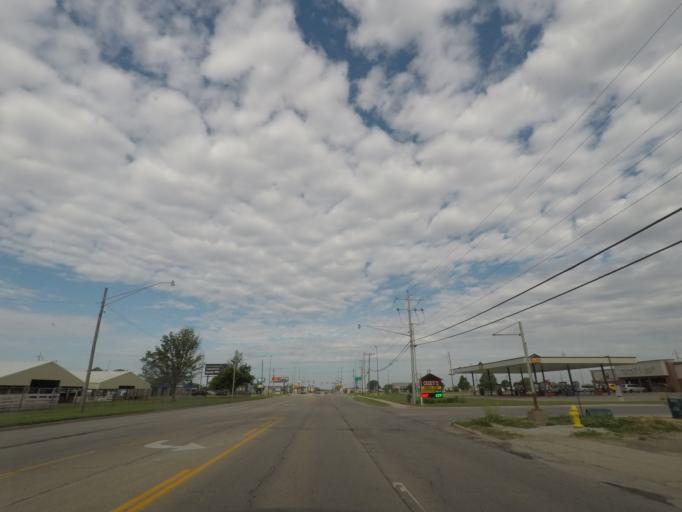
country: US
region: Illinois
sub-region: Logan County
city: Lincoln
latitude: 40.1578
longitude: -89.3841
